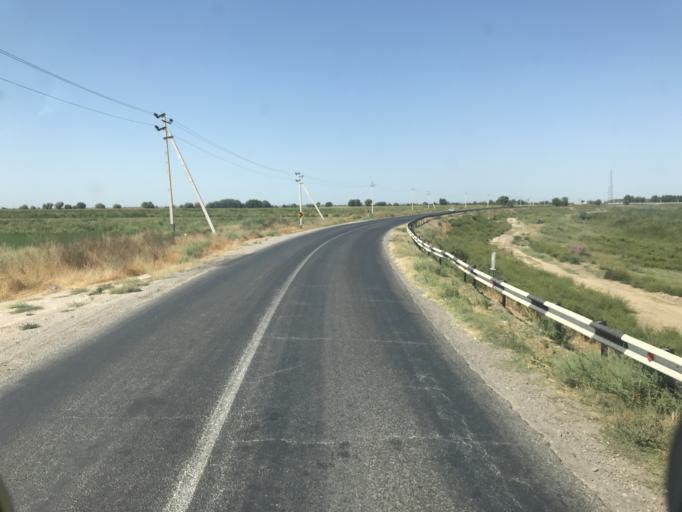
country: KZ
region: Ongtustik Qazaqstan
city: Ilyich
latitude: 40.9505
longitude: 68.4775
